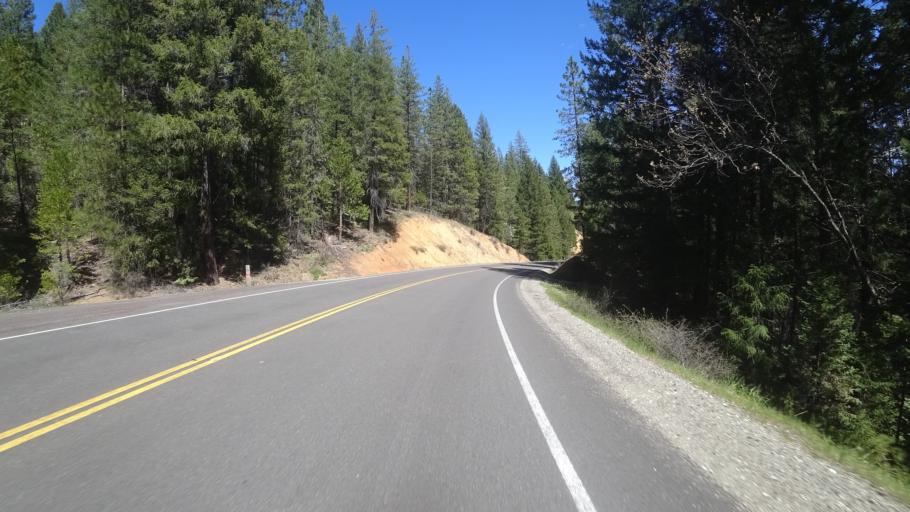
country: US
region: California
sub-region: Trinity County
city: Lewiston
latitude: 40.9061
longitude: -122.7862
